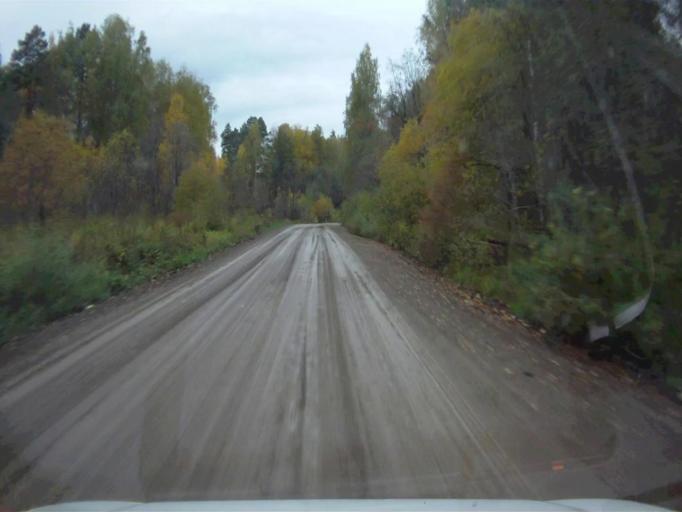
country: RU
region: Chelyabinsk
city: Nyazepetrovsk
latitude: 56.1004
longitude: 59.3902
